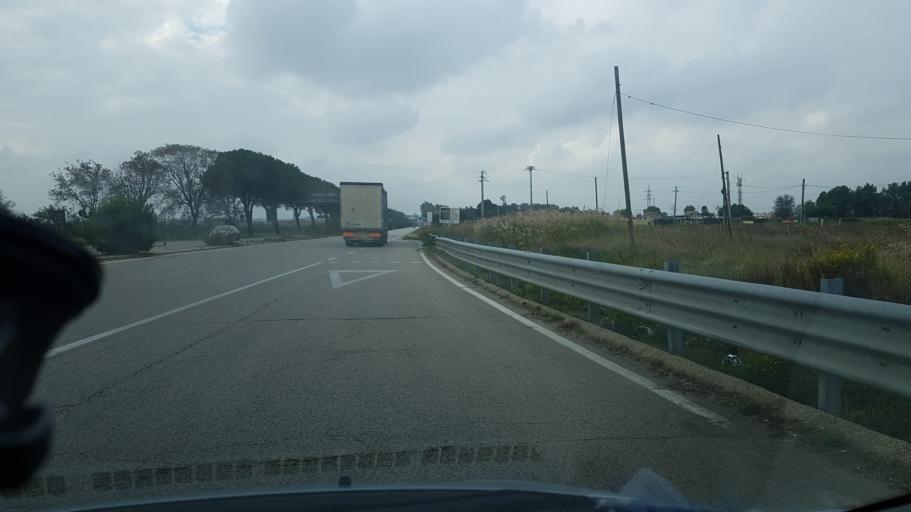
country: IT
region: Apulia
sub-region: Provincia di Foggia
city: Foggia
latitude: 41.4894
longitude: 15.5662
